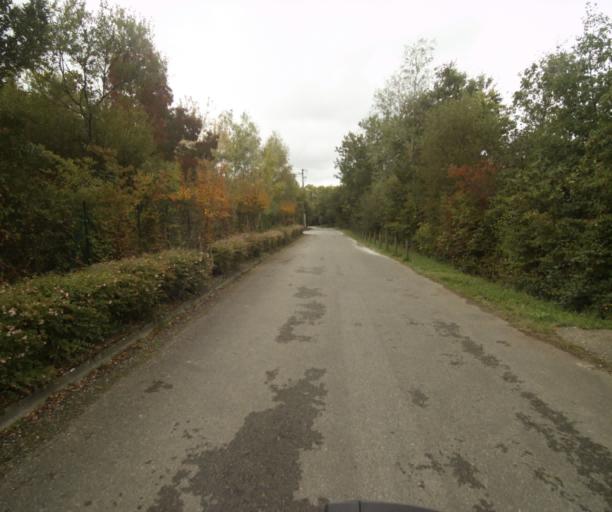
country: FR
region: Midi-Pyrenees
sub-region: Departement du Tarn-et-Garonne
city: Montech
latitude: 43.9646
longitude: 1.2383
